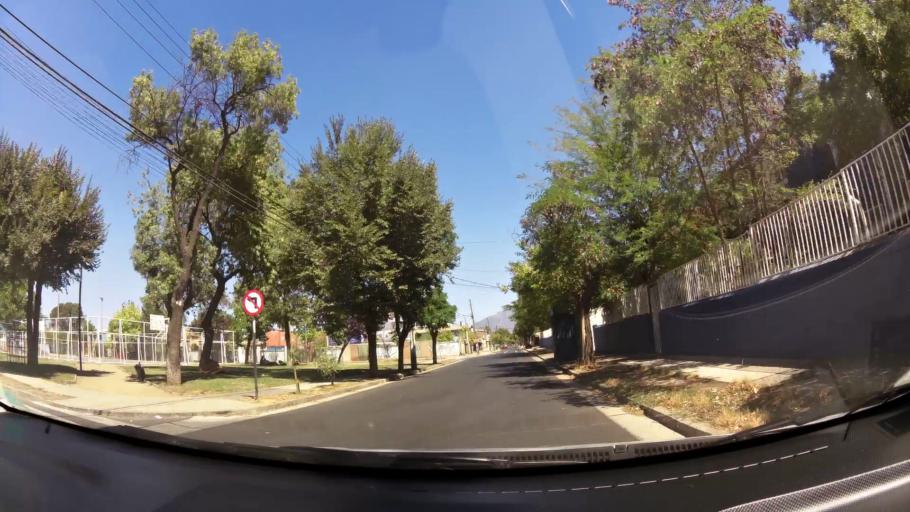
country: CL
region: O'Higgins
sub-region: Provincia de Cachapoal
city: Rancagua
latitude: -34.1707
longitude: -70.7298
